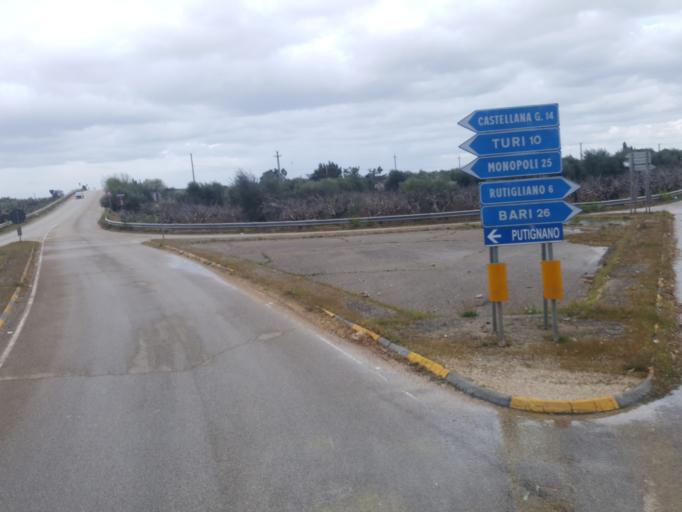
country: IT
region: Apulia
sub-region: Provincia di Bari
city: Conversano
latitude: 40.9815
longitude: 17.0905
